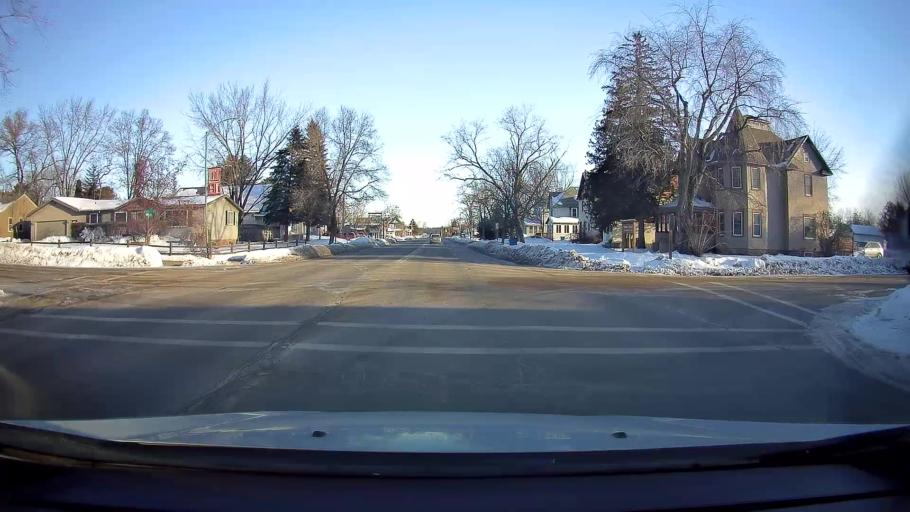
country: US
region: Wisconsin
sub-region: Washburn County
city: Spooner
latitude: 45.8303
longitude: -91.8857
